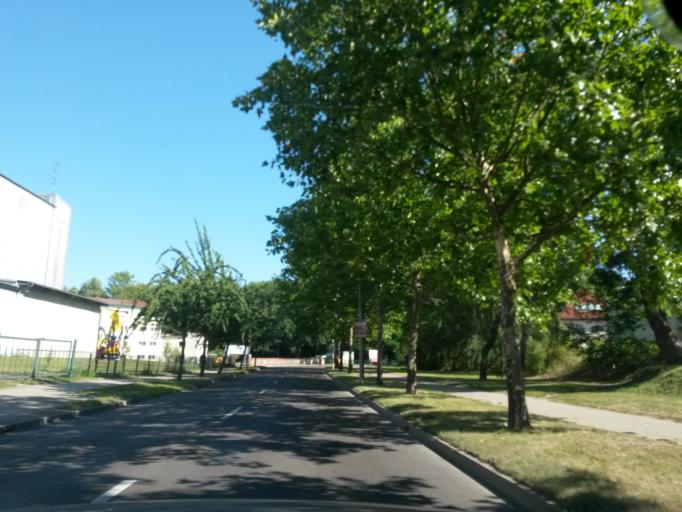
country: DE
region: Brandenburg
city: Prenzlau
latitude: 53.3046
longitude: 13.8243
